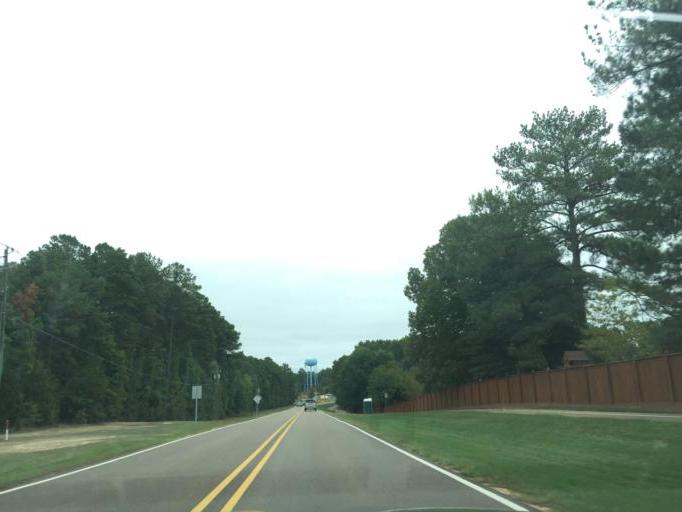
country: US
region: Mississippi
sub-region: Madison County
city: Madison
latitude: 32.4060
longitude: -90.0029
